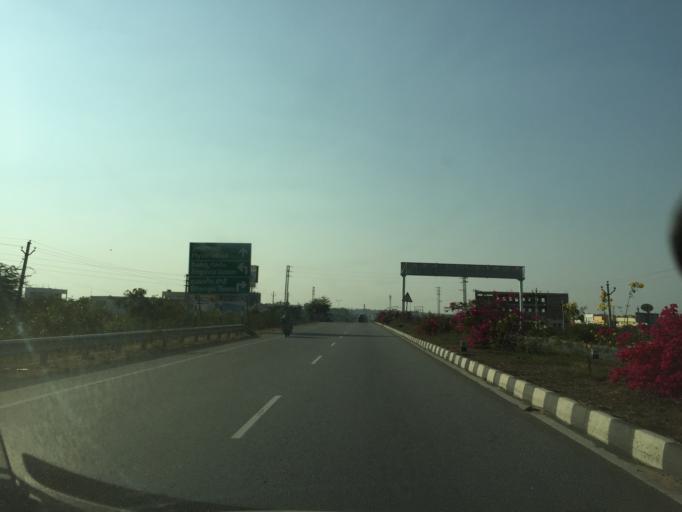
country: IN
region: Telangana
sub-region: Nalgonda
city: Bhongir
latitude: 17.5006
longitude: 78.8847
